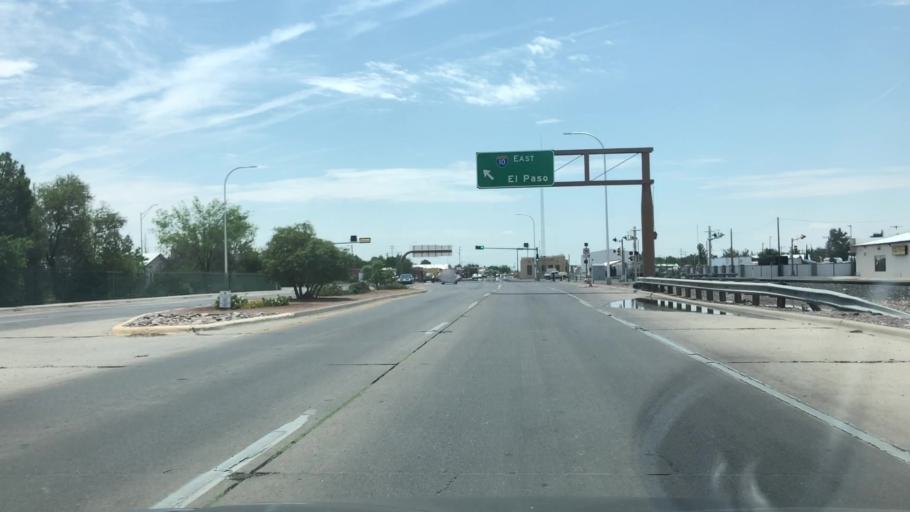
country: US
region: New Mexico
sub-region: Dona Ana County
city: University Park
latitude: 32.2785
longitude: -106.7687
